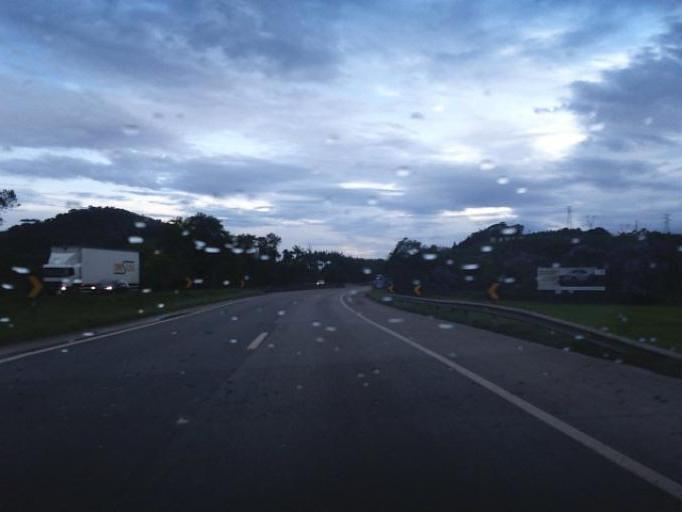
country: BR
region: Santa Catarina
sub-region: Joinville
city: Joinville
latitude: -26.1069
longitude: -48.8725
